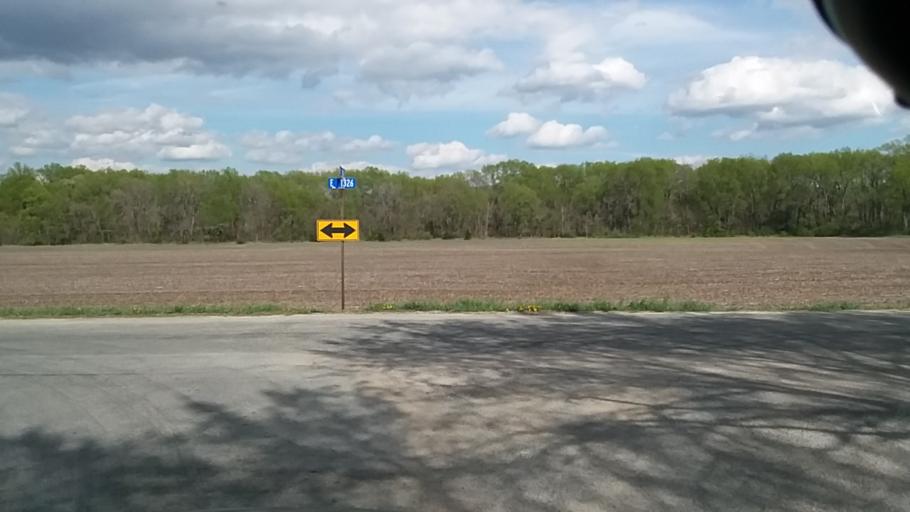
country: US
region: Kansas
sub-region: Douglas County
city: Lawrence
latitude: 38.8926
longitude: -95.2558
